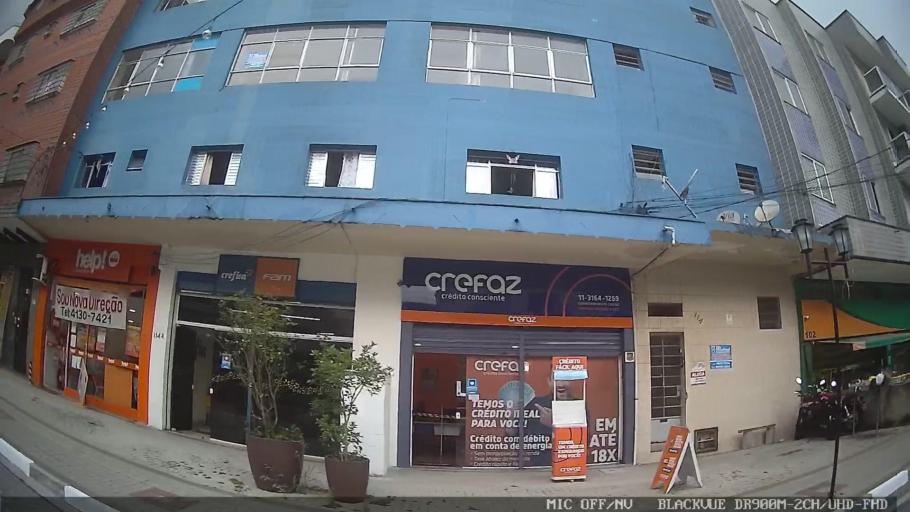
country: BR
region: Sao Paulo
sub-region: Ribeirao Pires
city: Ribeirao Pires
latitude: -23.7105
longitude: -46.4130
